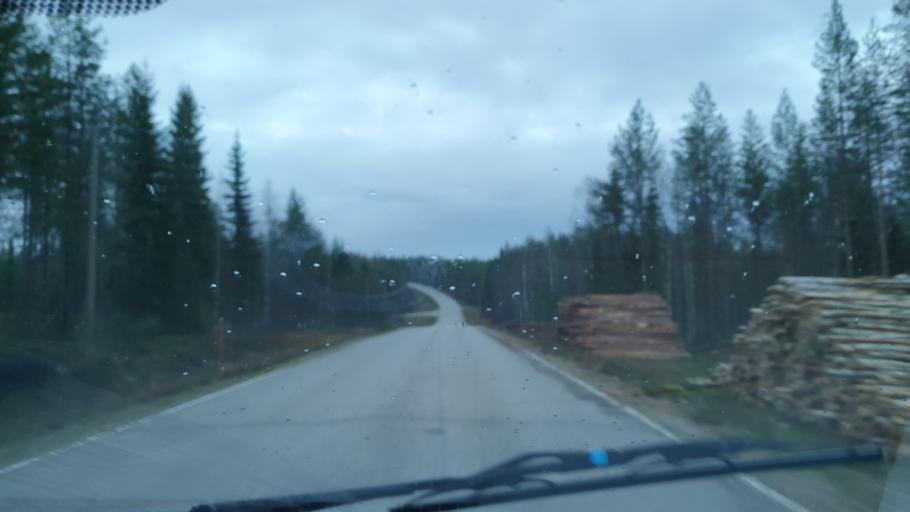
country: FI
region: Kainuu
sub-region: Kajaani
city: Ristijaervi
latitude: 64.4365
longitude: 28.3682
